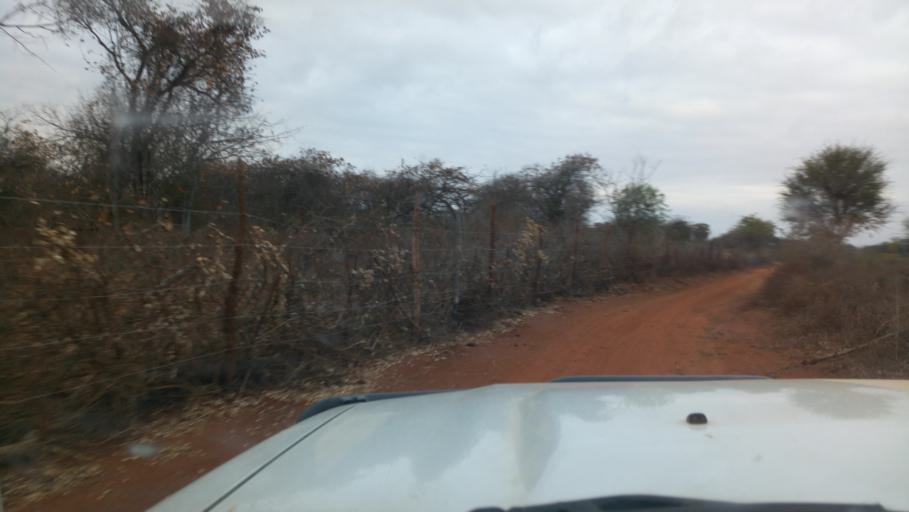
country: KE
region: Kitui
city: Kitui
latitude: -1.8601
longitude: 38.2160
